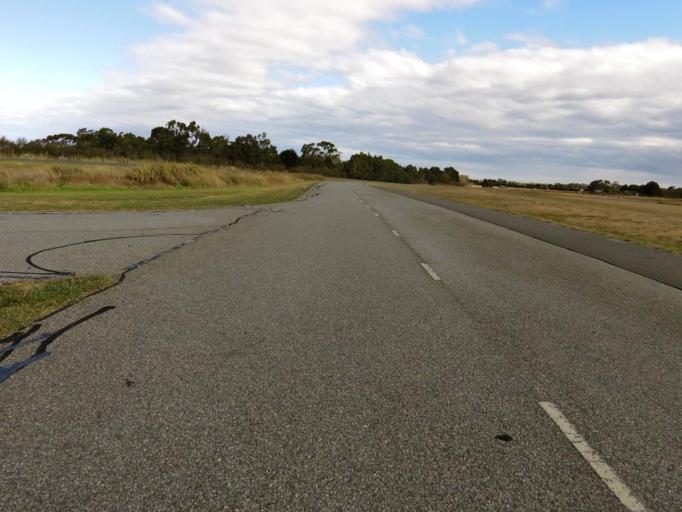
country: AU
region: Victoria
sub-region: Casey
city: Cranbourne East
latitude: -38.1261
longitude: 145.3155
